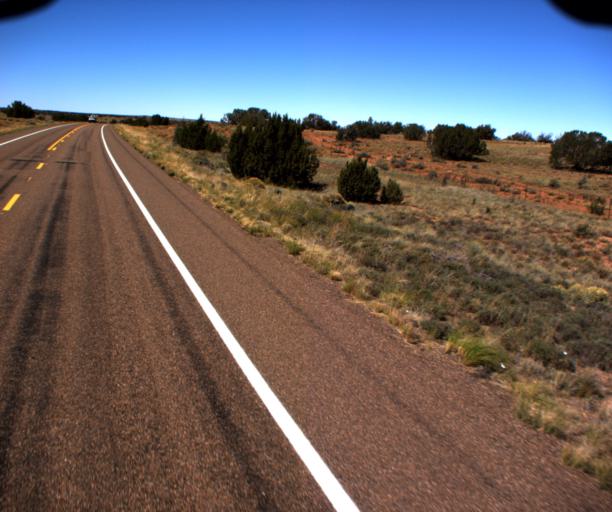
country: US
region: Arizona
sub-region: Apache County
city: Saint Johns
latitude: 34.5989
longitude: -109.6353
